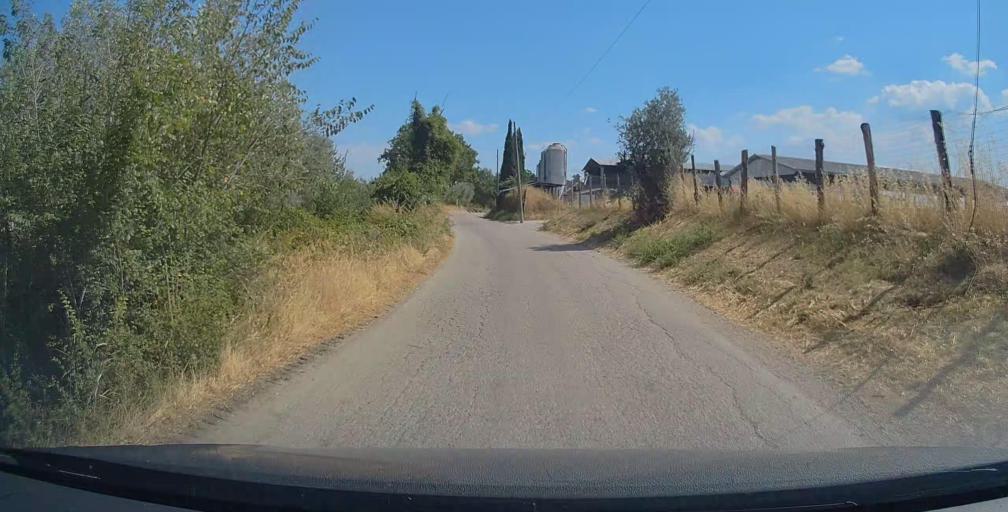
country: IT
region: Umbria
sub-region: Provincia di Terni
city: Calvi dell'Umbria
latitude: 42.3876
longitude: 12.5676
